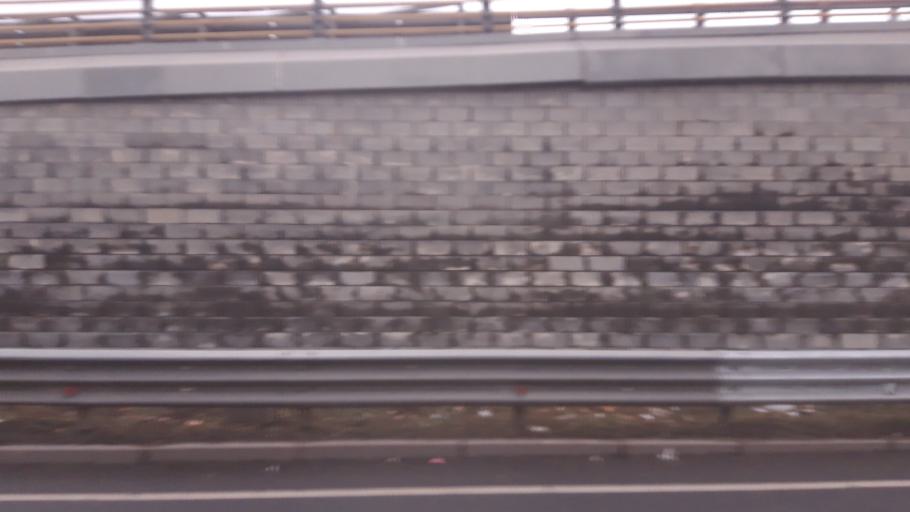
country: RU
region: St.-Petersburg
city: Kupchino
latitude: 59.8077
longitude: 30.3234
